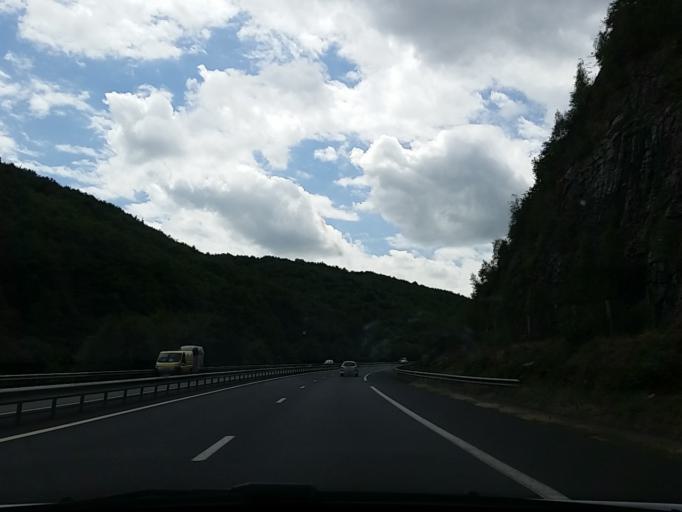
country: FR
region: Auvergne
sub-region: Departement du Cantal
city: Massiac
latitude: 45.1884
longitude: 3.1833
